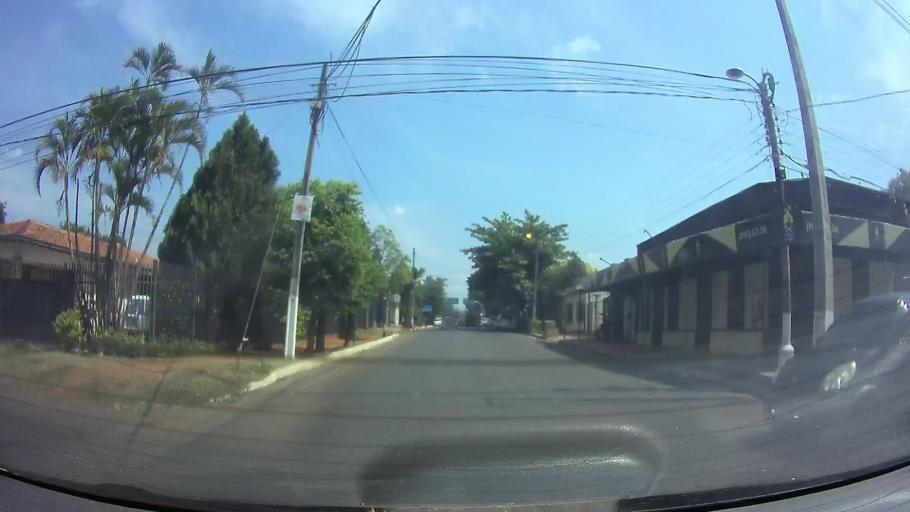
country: PY
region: Central
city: San Lorenzo
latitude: -25.3482
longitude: -57.4935
